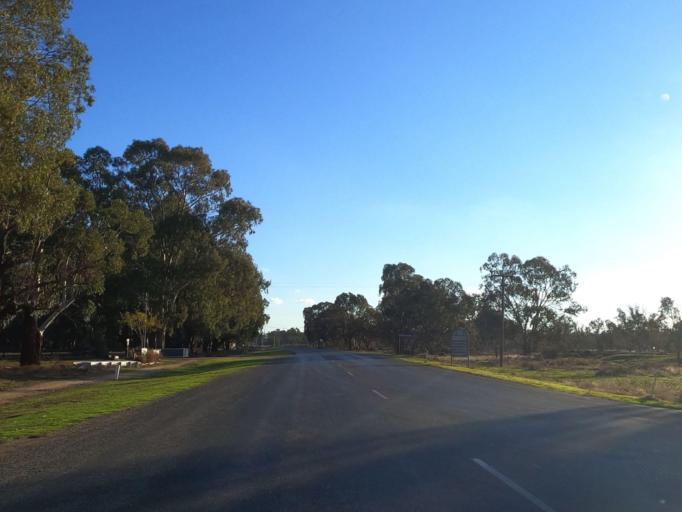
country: AU
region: Victoria
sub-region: Swan Hill
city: Swan Hill
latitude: -35.3361
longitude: 143.5762
